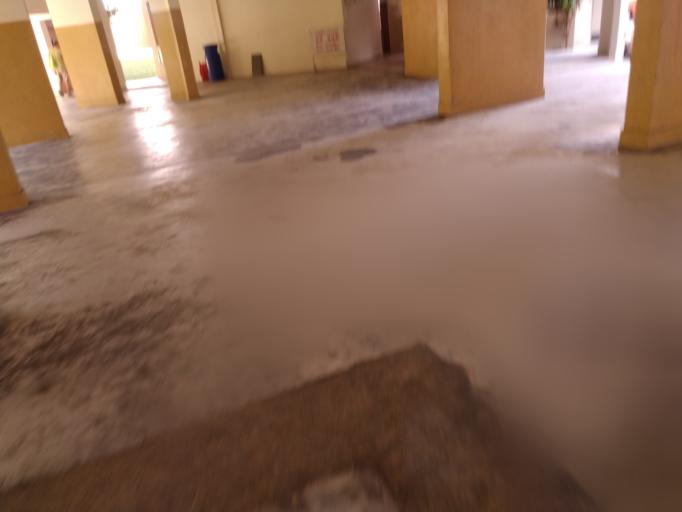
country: SG
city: Singapore
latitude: 1.2872
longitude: 103.8119
